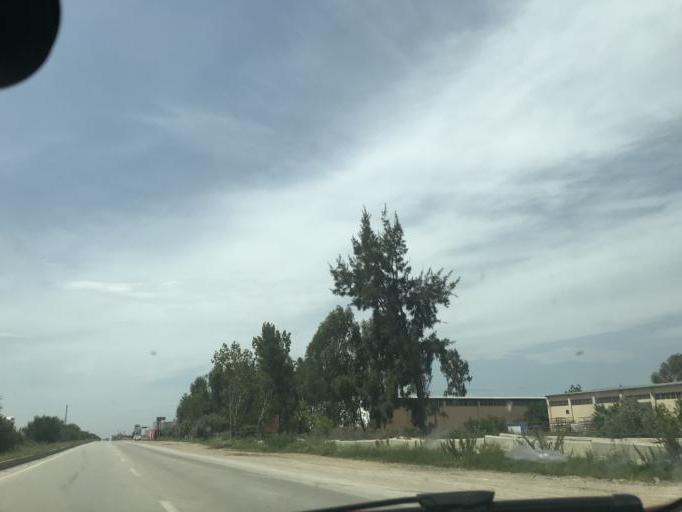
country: TR
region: Adana
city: Yakapinar
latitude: 36.9732
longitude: 35.5064
